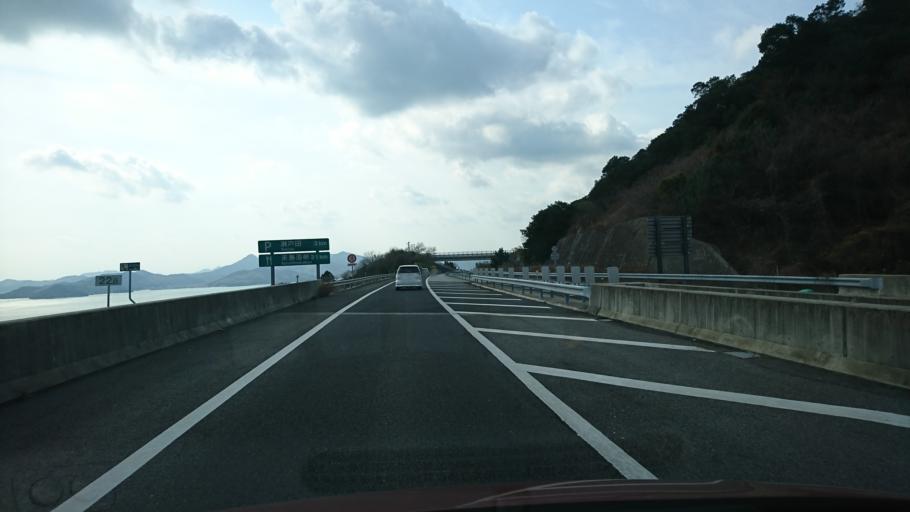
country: JP
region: Hiroshima
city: Innoshima
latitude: 34.2760
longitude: 133.1073
